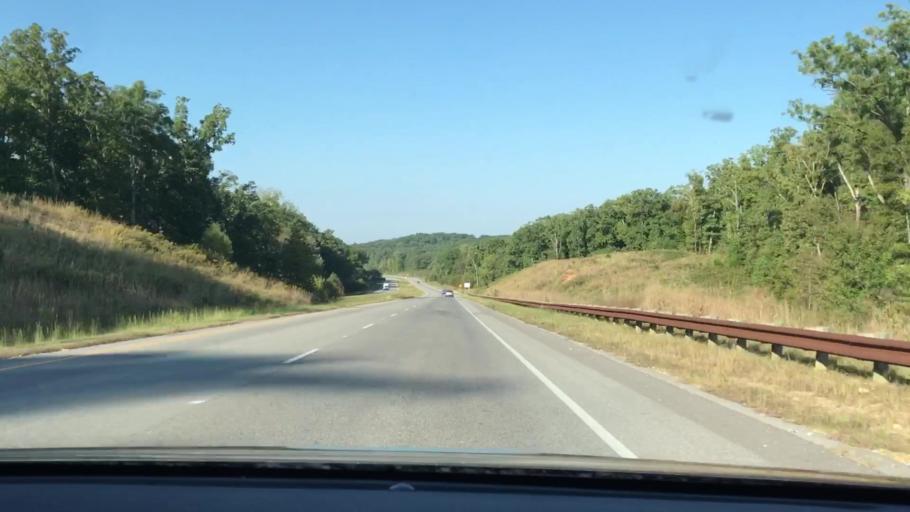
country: US
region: Kentucky
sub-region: Trigg County
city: Cadiz
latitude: 36.7797
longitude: -88.0883
